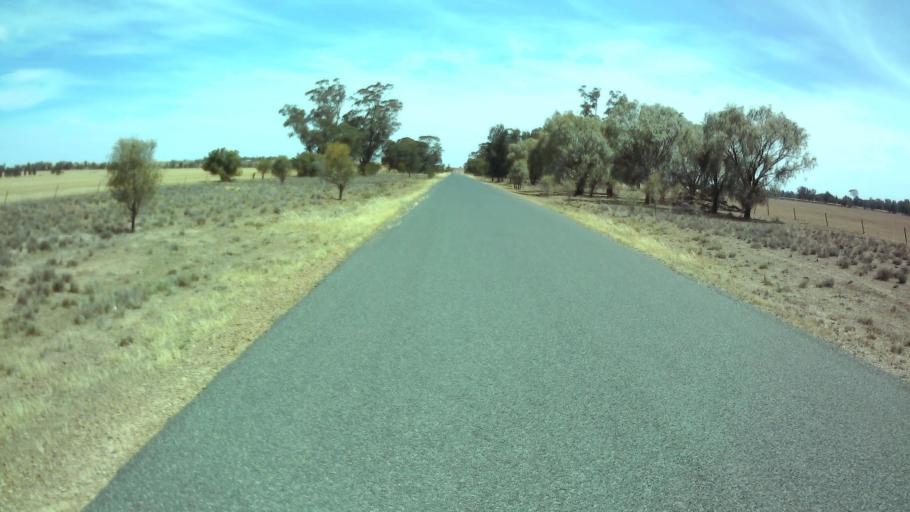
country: AU
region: New South Wales
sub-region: Weddin
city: Grenfell
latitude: -33.8803
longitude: 147.7430
